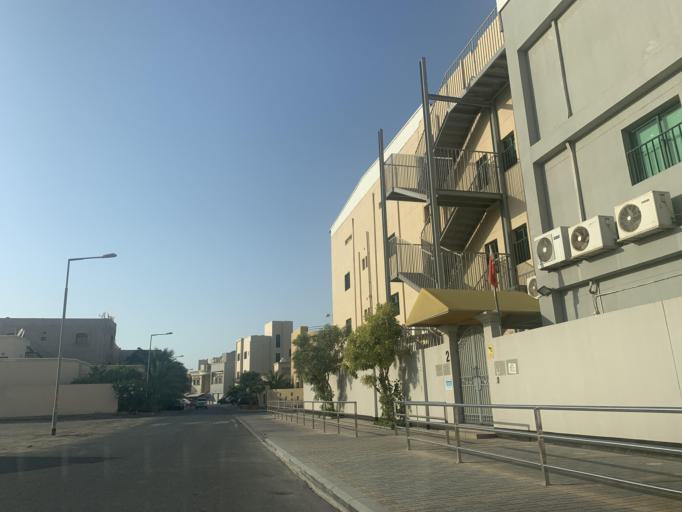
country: BH
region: Manama
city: Jidd Hafs
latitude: 26.2128
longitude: 50.5272
